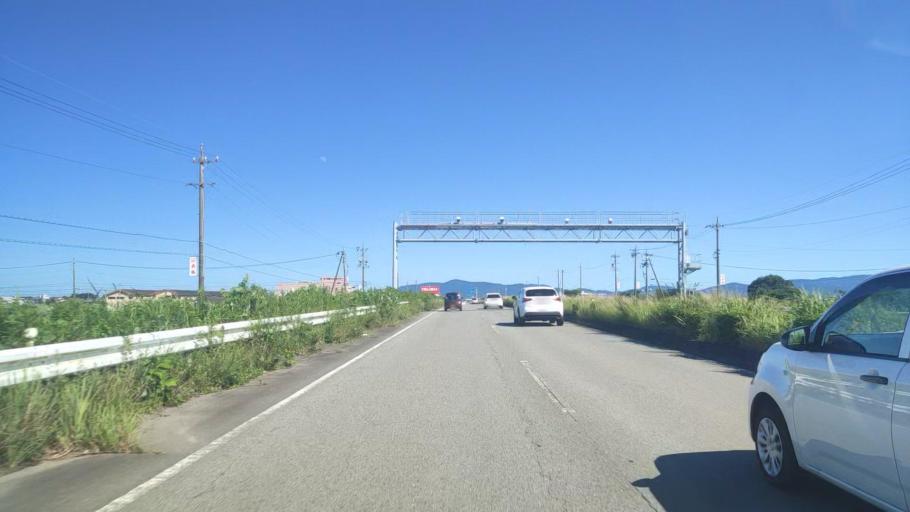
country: JP
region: Mie
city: Ise
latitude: 34.5588
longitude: 136.6469
